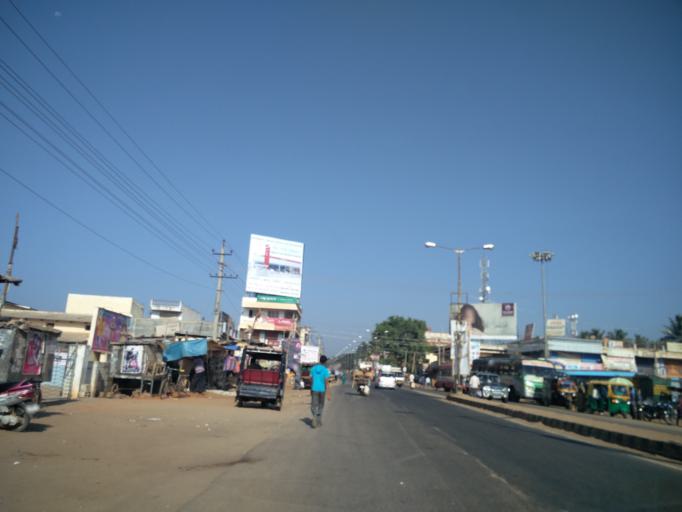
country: IN
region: Karnataka
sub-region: Tumkur
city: Gubbi
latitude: 13.3091
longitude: 76.9435
